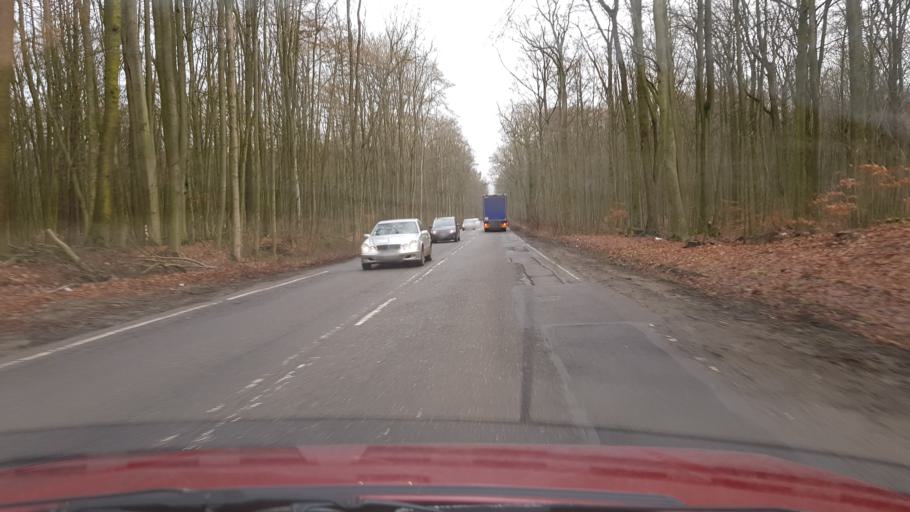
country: PL
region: West Pomeranian Voivodeship
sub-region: Powiat policki
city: Police
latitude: 53.5294
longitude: 14.5728
